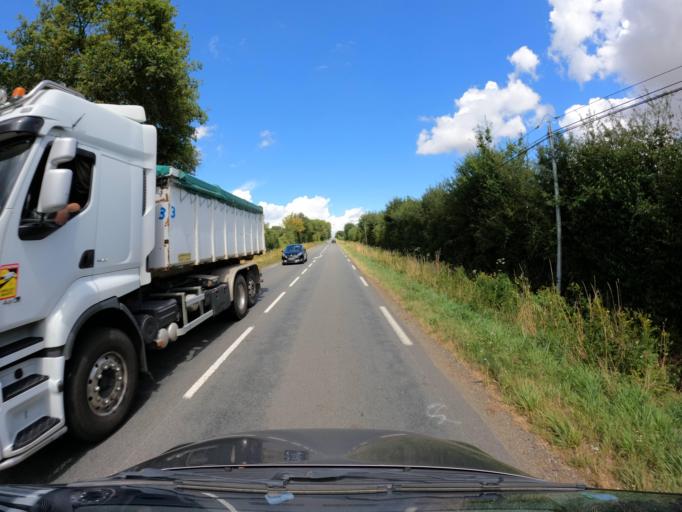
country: FR
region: Pays de la Loire
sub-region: Departement de la Sarthe
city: Juigne-sur-Sarthe
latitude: 47.8917
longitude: -0.2902
